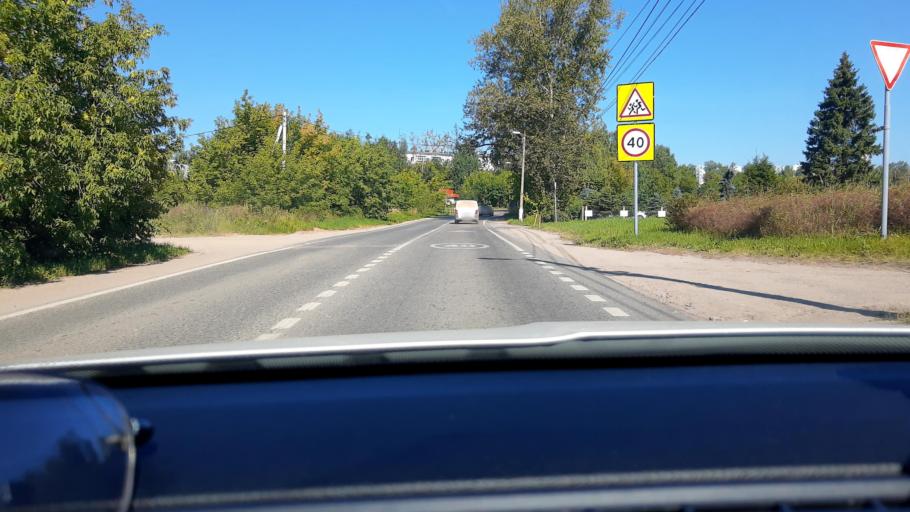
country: RU
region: Moskovskaya
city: Petrovo-Dal'neye
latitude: 55.7662
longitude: 37.2231
